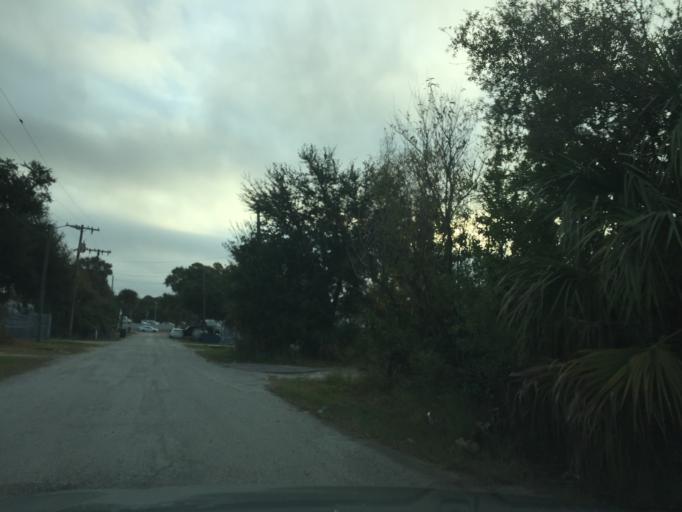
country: US
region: Florida
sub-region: Hillsborough County
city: Town 'n' Country
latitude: 27.9847
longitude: -82.5484
